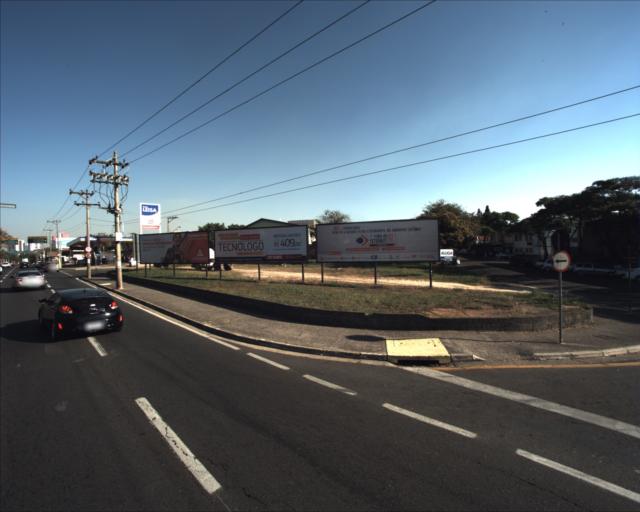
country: BR
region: Sao Paulo
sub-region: Sorocaba
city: Sorocaba
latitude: -23.4816
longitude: -47.4393
